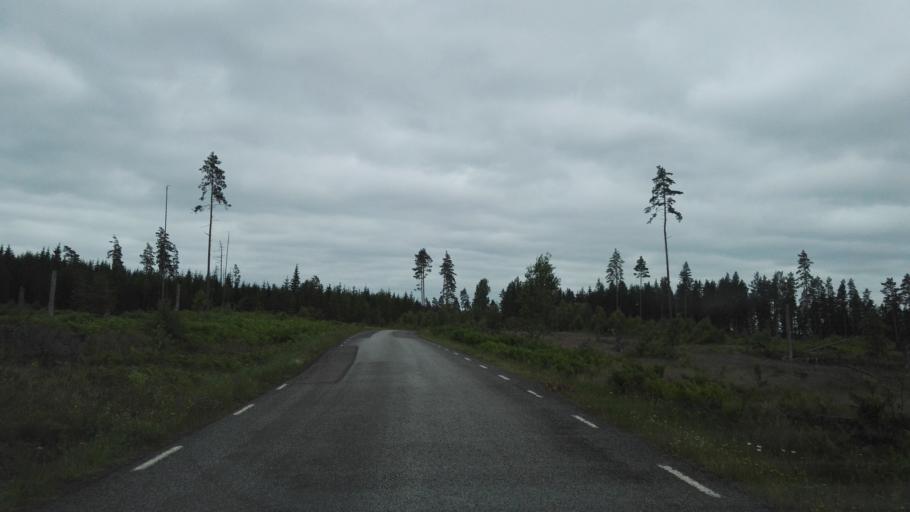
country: SE
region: Kronoberg
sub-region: Vaxjo Kommun
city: Rottne
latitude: 57.1298
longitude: 14.8122
